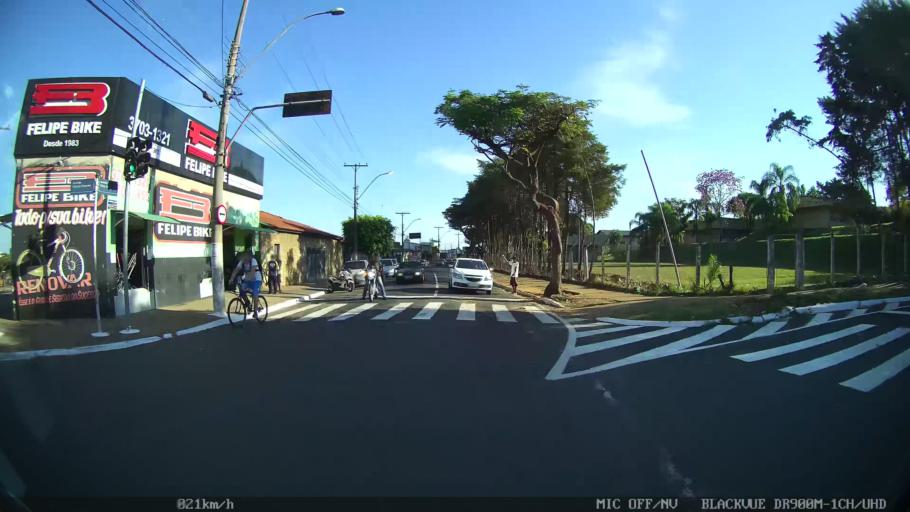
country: BR
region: Sao Paulo
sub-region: Franca
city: Franca
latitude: -20.5099
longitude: -47.4003
